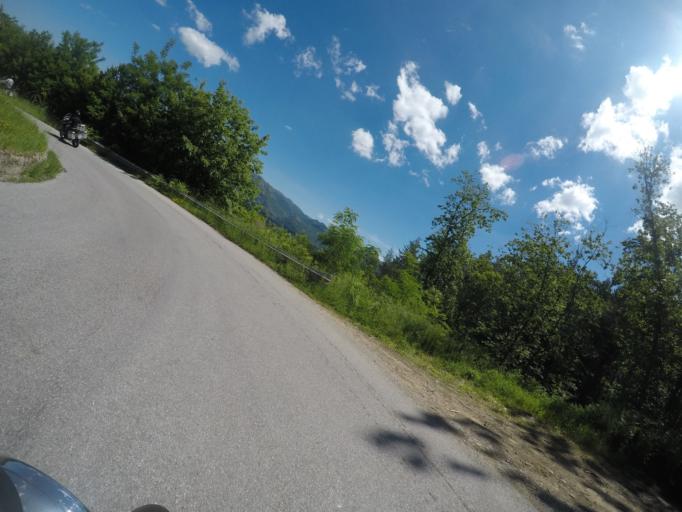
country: IT
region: Tuscany
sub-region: Provincia di Lucca
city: Careggine
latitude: 44.1345
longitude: 10.3400
